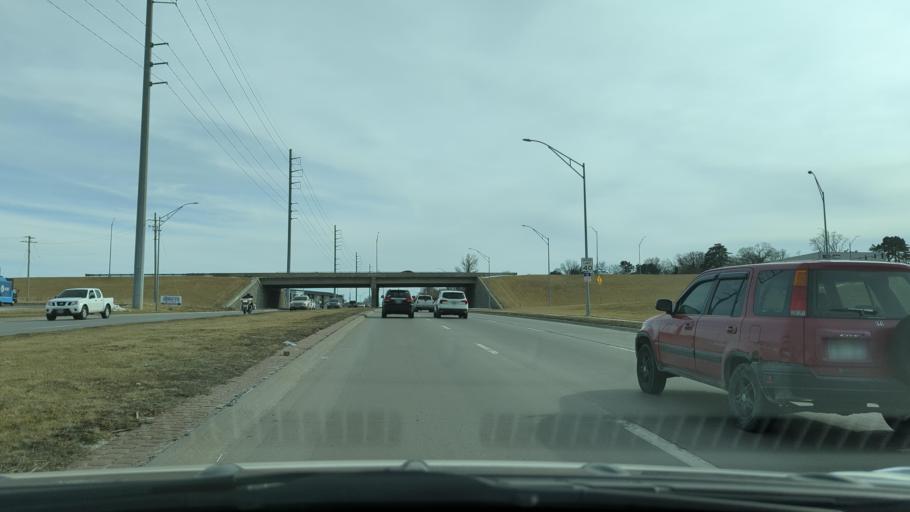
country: US
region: Nebraska
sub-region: Douglas County
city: Ralston
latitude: 41.2363
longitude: -96.0244
